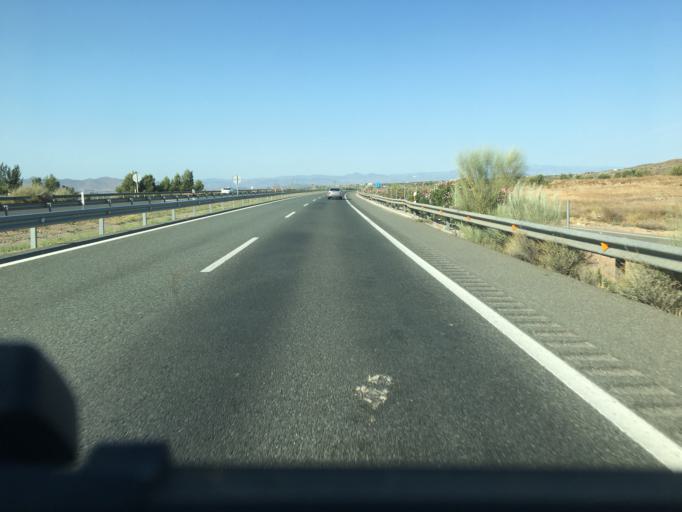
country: ES
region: Murcia
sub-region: Murcia
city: Puerto Lumbreras
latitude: 37.4904
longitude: -1.8538
